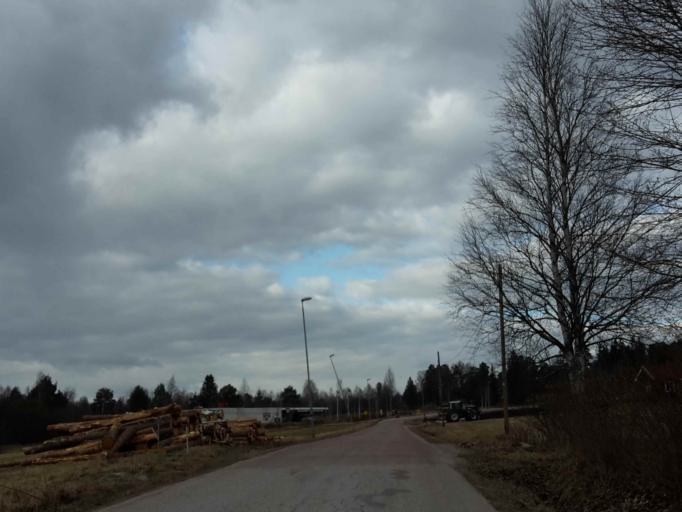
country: SE
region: Dalarna
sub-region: Orsa Kommun
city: Orsa
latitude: 61.1052
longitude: 14.6276
